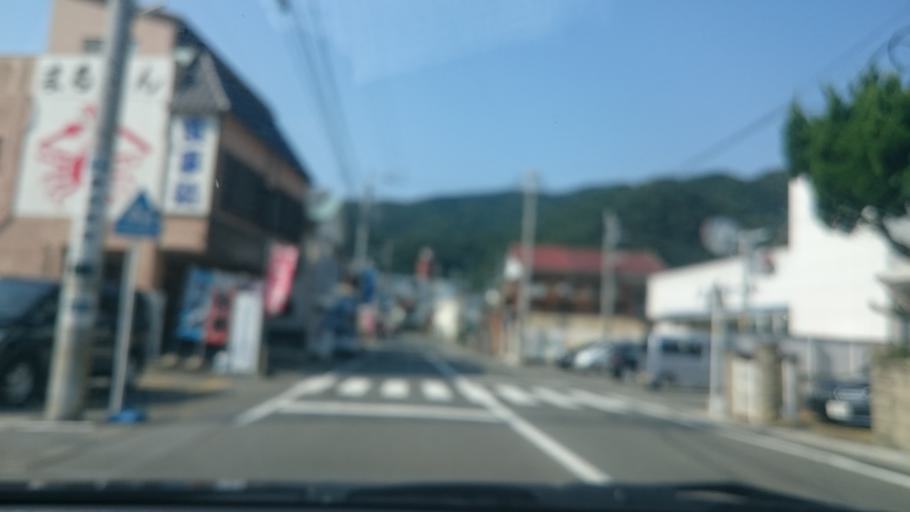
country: JP
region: Shizuoka
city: Heda
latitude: 34.9709
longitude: 138.7776
